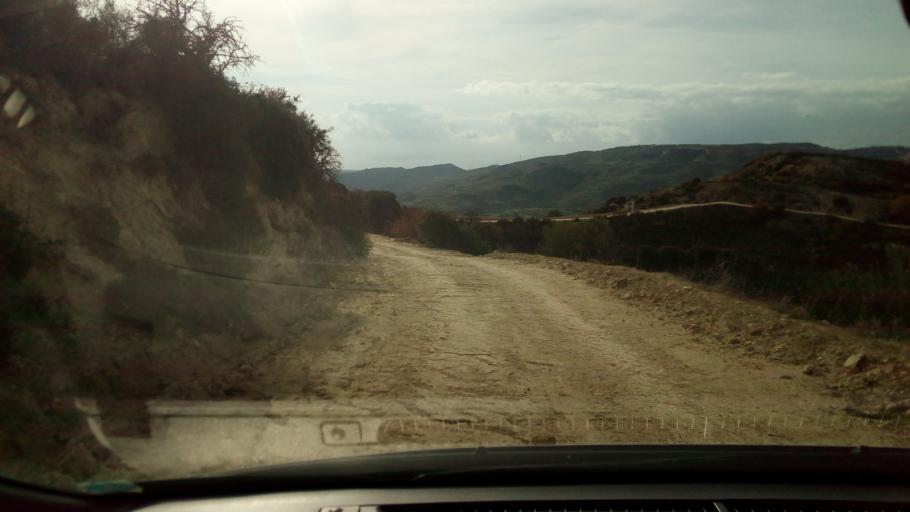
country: CY
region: Pafos
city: Mesogi
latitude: 34.7990
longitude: 32.5425
